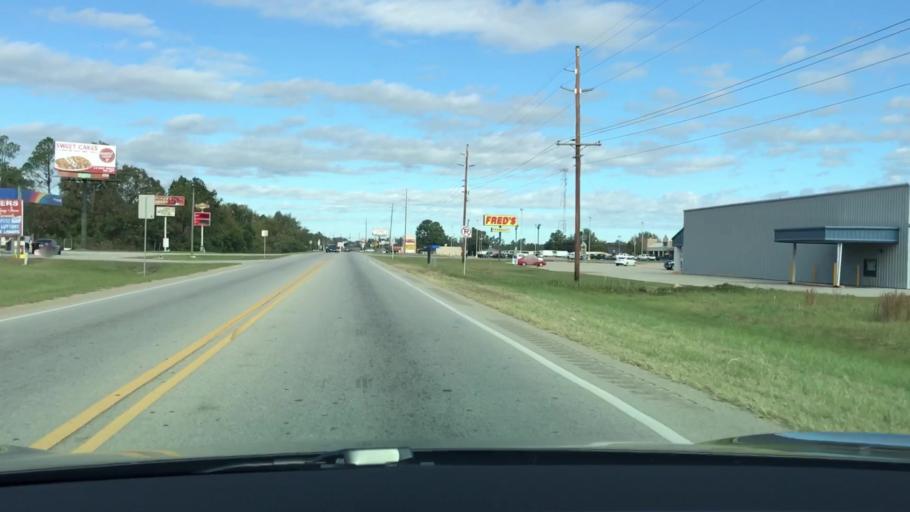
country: US
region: Georgia
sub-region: Jefferson County
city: Louisville
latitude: 33.0072
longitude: -82.3967
